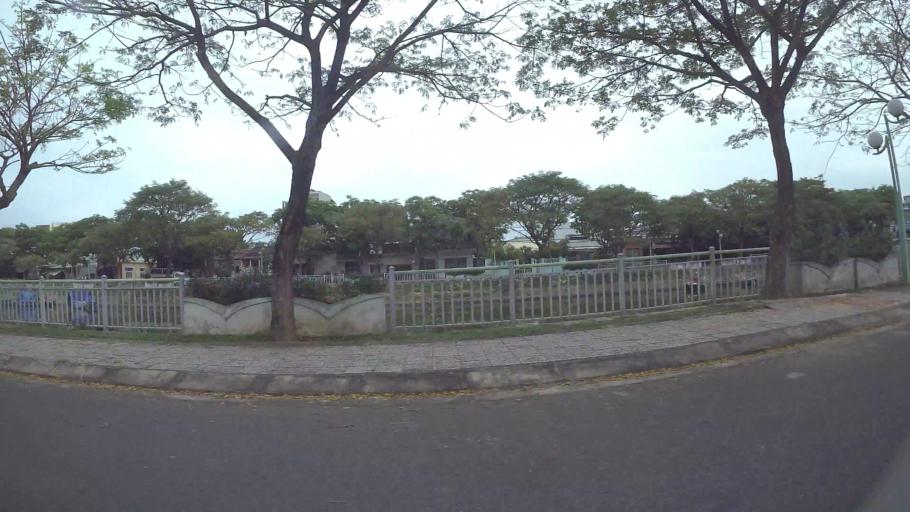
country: VN
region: Da Nang
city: Thanh Khe
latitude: 16.0711
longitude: 108.1820
